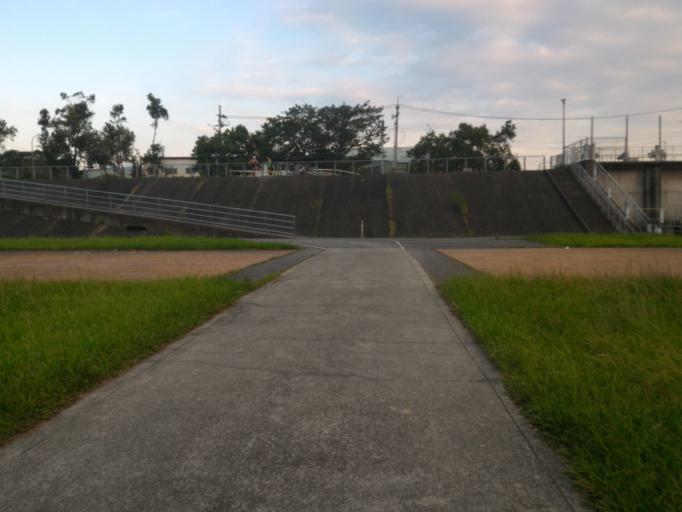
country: TW
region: Taipei
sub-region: Taipei
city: Banqiao
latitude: 24.9723
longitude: 121.4196
